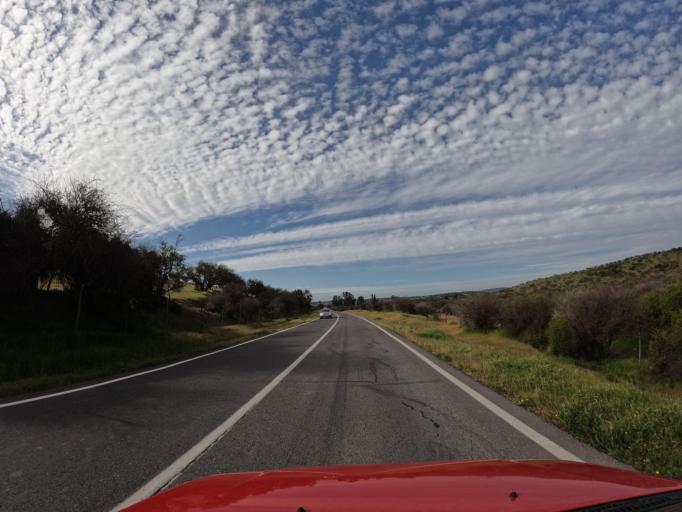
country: CL
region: O'Higgins
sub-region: Provincia de Colchagua
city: Santa Cruz
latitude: -34.2973
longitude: -71.7322
